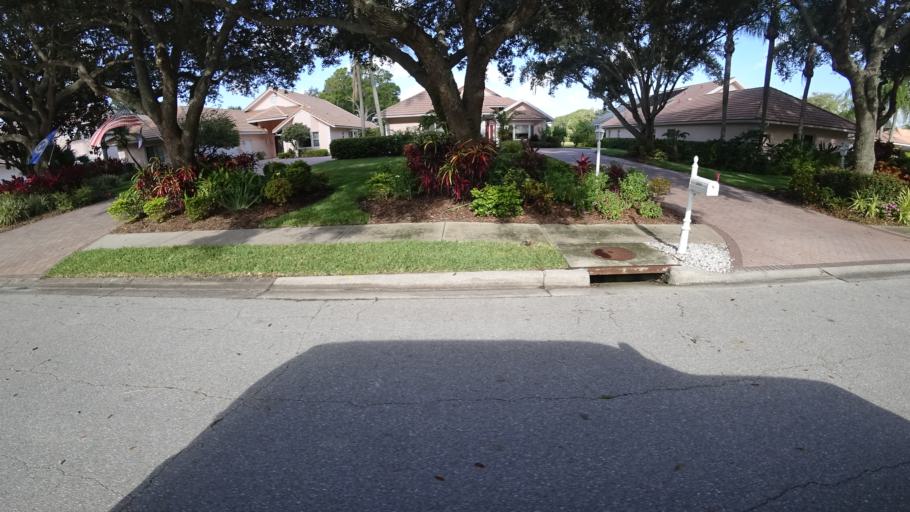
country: US
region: Florida
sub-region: Sarasota County
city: Desoto Lakes
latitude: 27.4111
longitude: -82.4935
